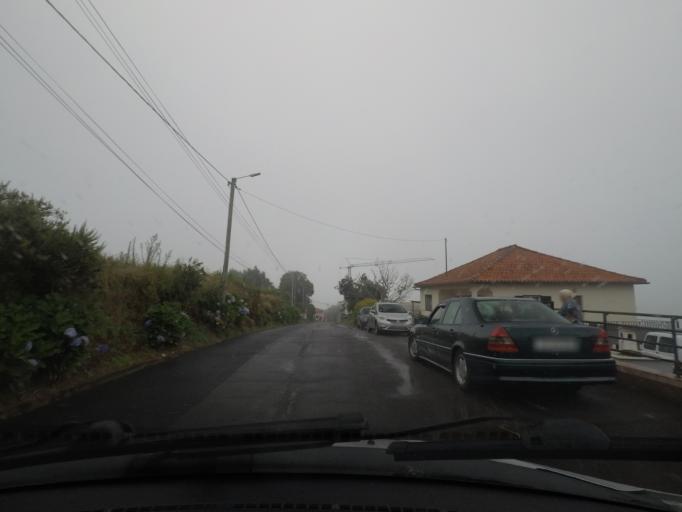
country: PT
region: Madeira
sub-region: Santana
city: Santana
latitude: 32.7987
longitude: -16.8773
